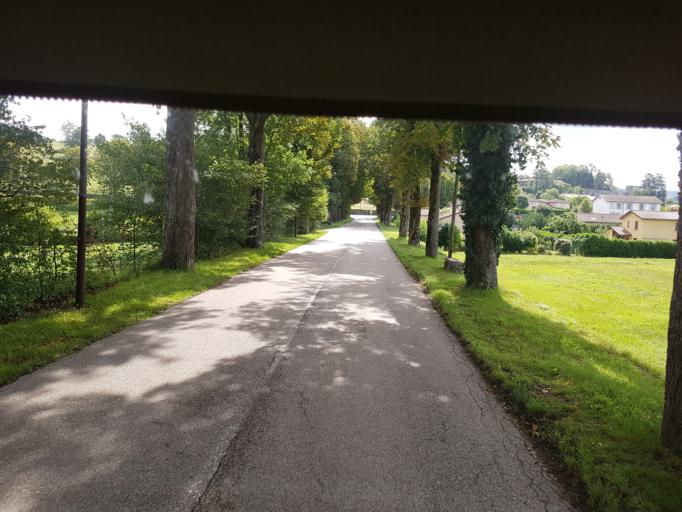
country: FR
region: Rhone-Alpes
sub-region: Departement de l'Ain
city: Poncin
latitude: 46.0895
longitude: 5.4050
